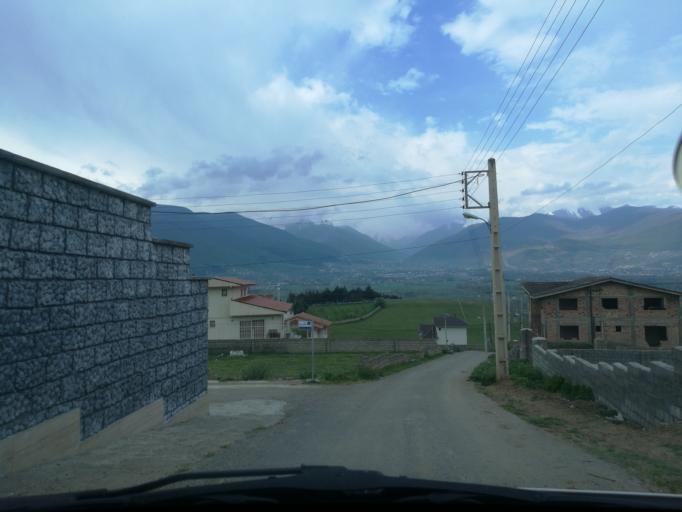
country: IR
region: Mazandaran
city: `Abbasabad
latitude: 36.5346
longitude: 51.2243
